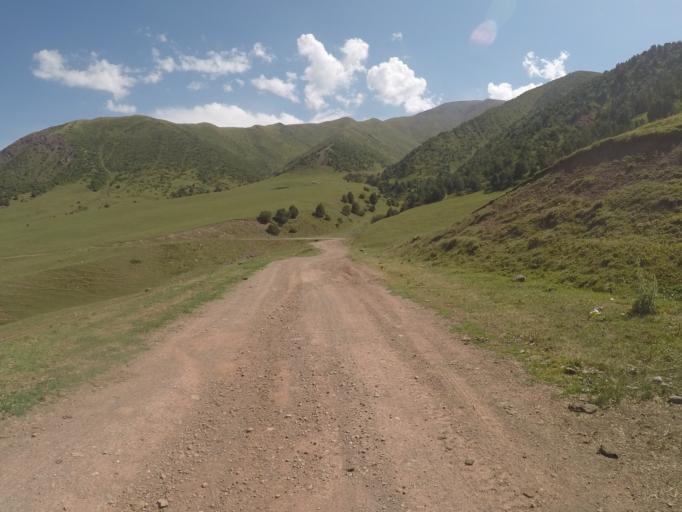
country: KG
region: Chuy
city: Bishkek
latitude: 42.6446
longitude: 74.5701
